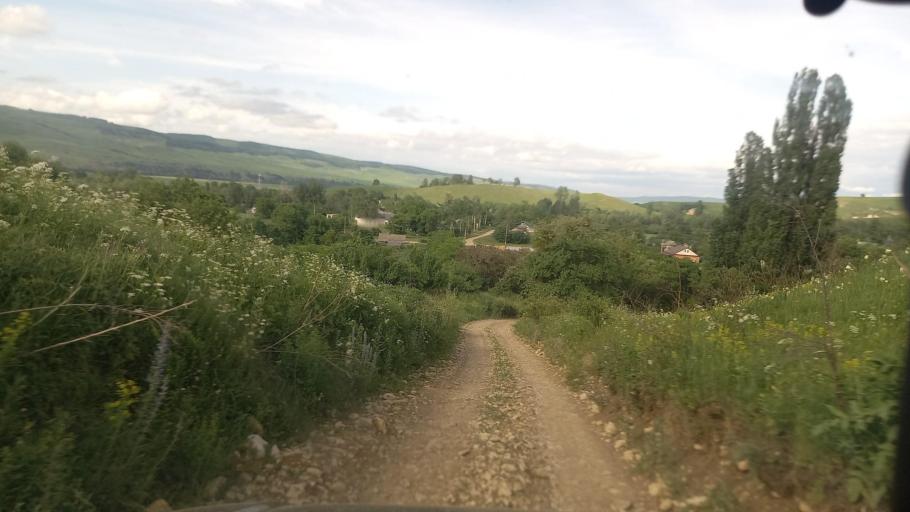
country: RU
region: Krasnodarskiy
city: Peredovaya
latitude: 44.0812
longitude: 41.3657
